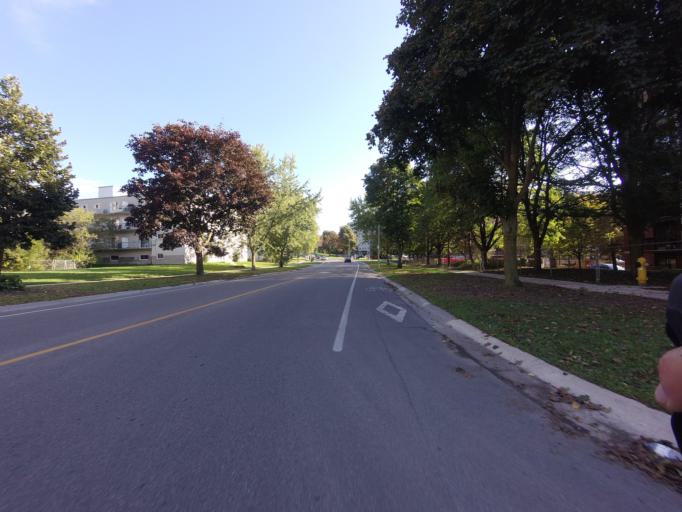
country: CA
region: Ontario
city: Kingston
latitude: 44.2366
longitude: -76.5354
